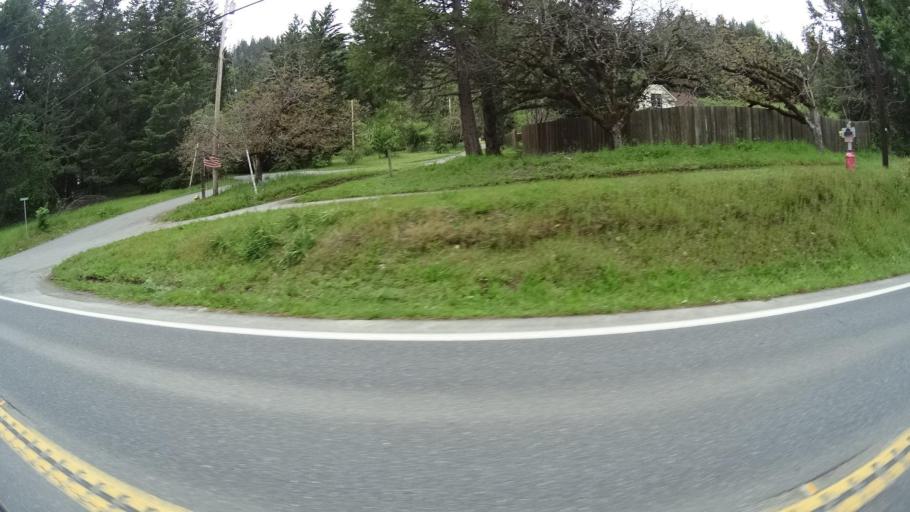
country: US
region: California
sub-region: Humboldt County
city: Willow Creek
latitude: 40.9651
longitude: -123.6416
